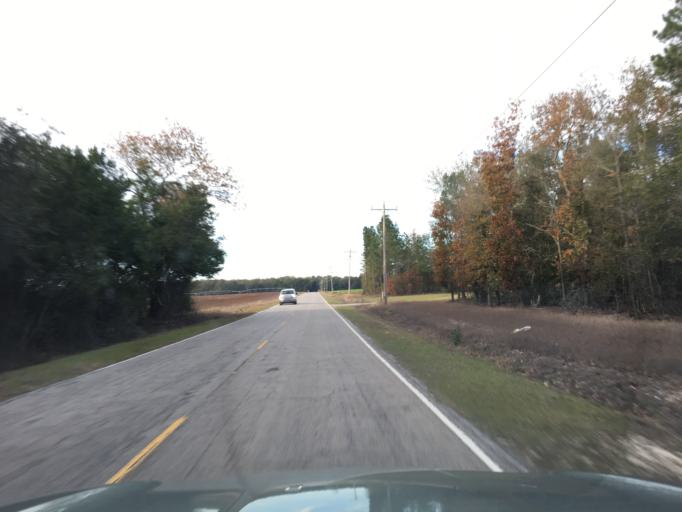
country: US
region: South Carolina
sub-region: Lexington County
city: Red Bank
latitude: 33.7503
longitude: -81.3655
